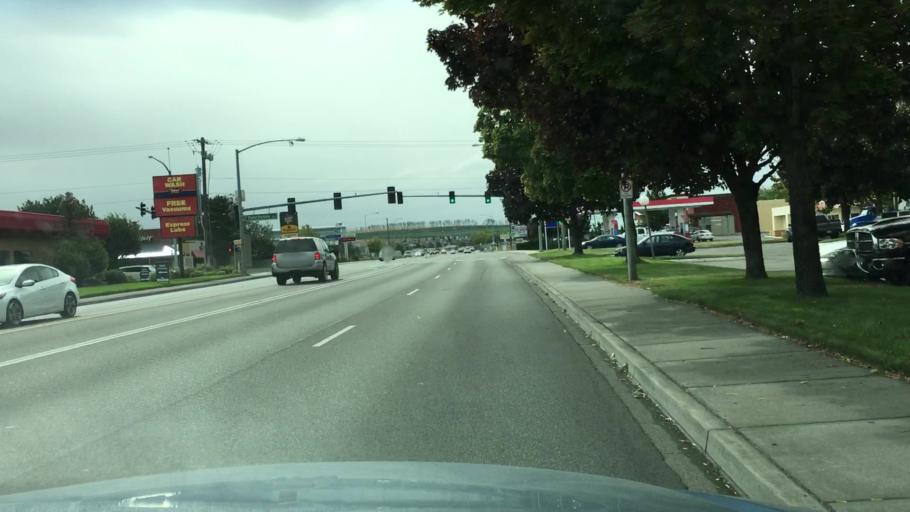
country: US
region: Washington
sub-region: Franklin County
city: West Pasco
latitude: 46.2133
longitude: -119.2257
